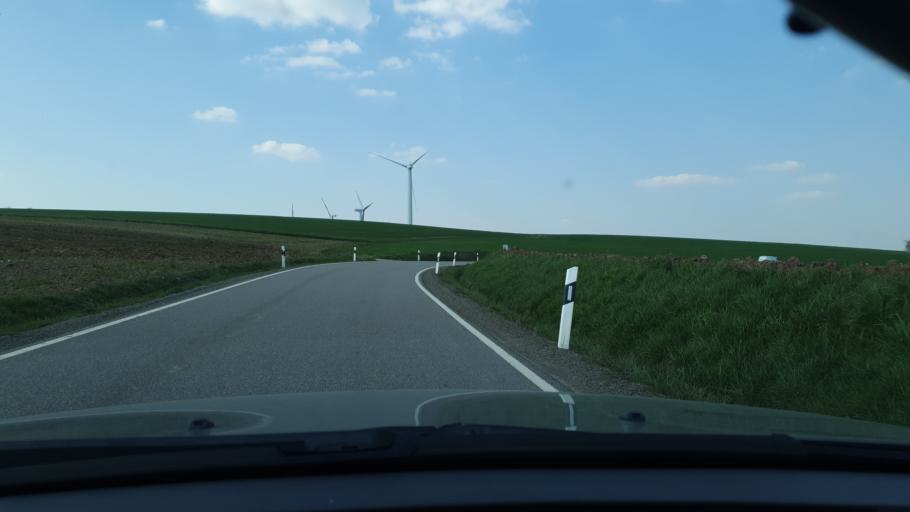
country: DE
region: Rheinland-Pfalz
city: Knopp-Labach
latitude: 49.3289
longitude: 7.4957
